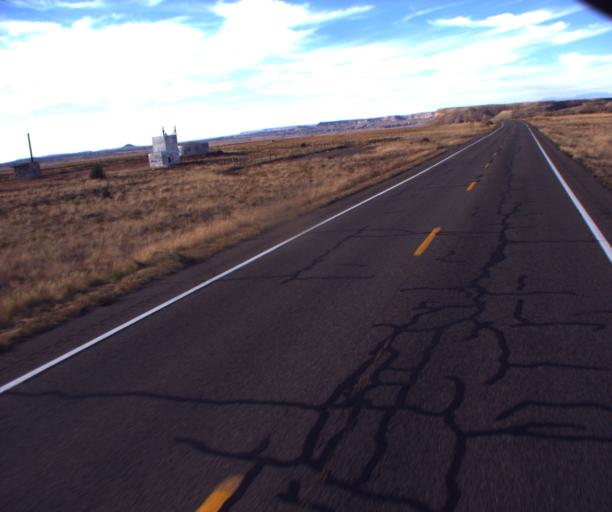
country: US
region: New Mexico
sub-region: San Juan County
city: Shiprock
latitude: 36.9082
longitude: -109.0714
